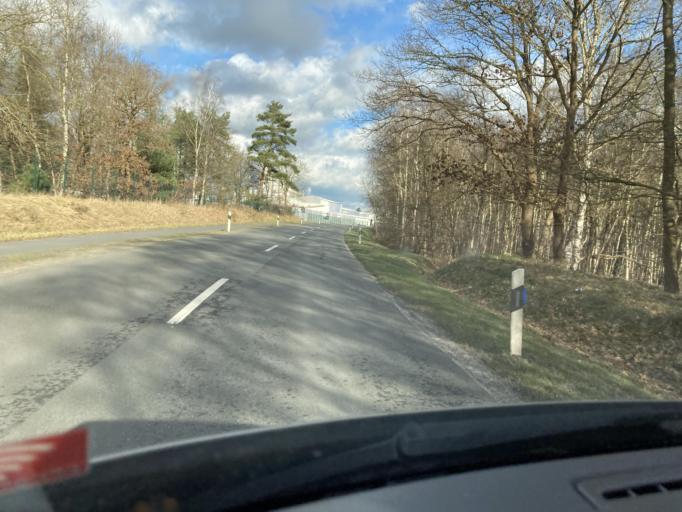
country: DE
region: Lower Saxony
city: Zetel
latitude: 53.4256
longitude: 7.9093
